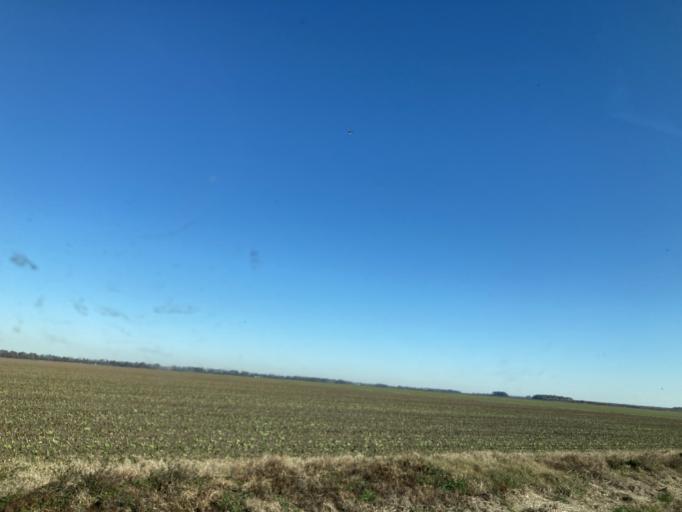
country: US
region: Mississippi
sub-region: Sharkey County
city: Rolling Fork
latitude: 32.8499
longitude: -90.6909
